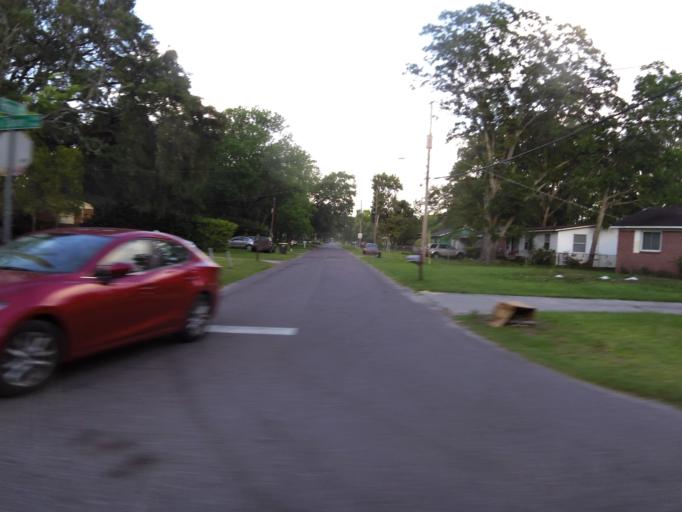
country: US
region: Florida
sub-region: Duval County
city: Jacksonville
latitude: 30.2979
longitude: -81.7390
